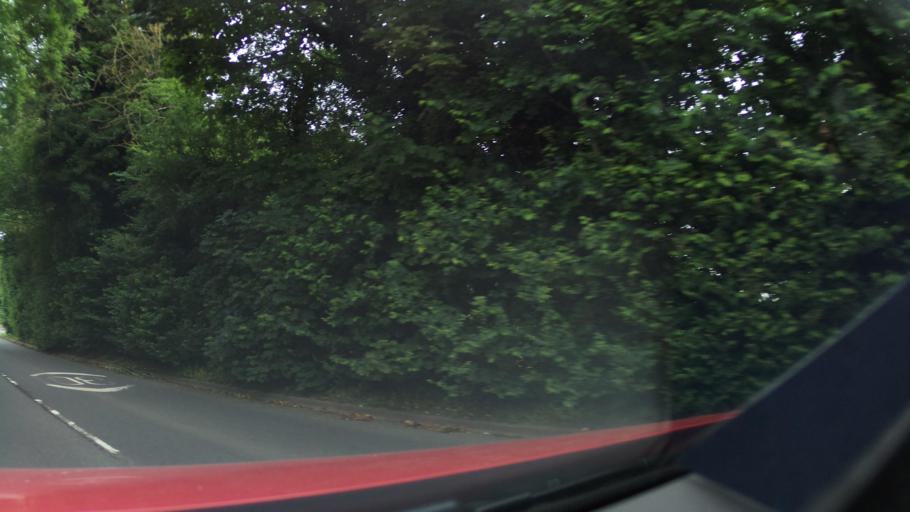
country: GB
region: England
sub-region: District of Rutland
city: Edith Weston
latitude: 52.6372
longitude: -0.6277
